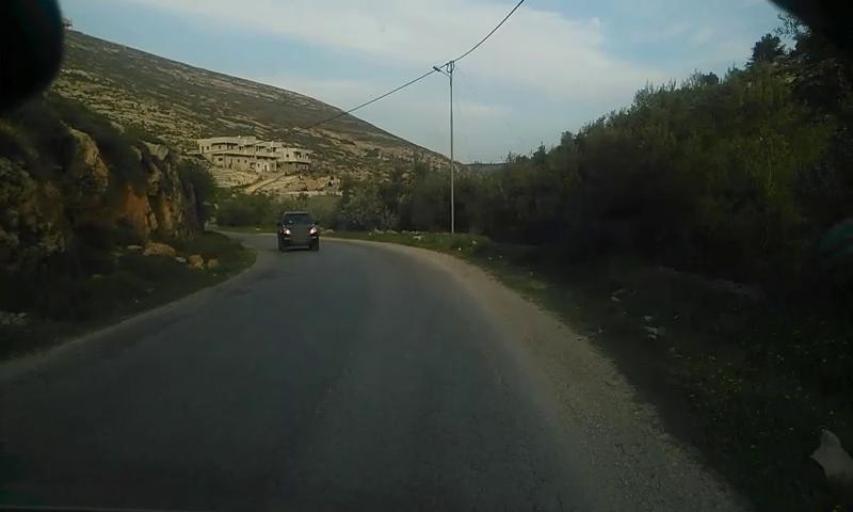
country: PS
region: West Bank
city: Ash Shuyukh
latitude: 31.5923
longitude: 35.1627
